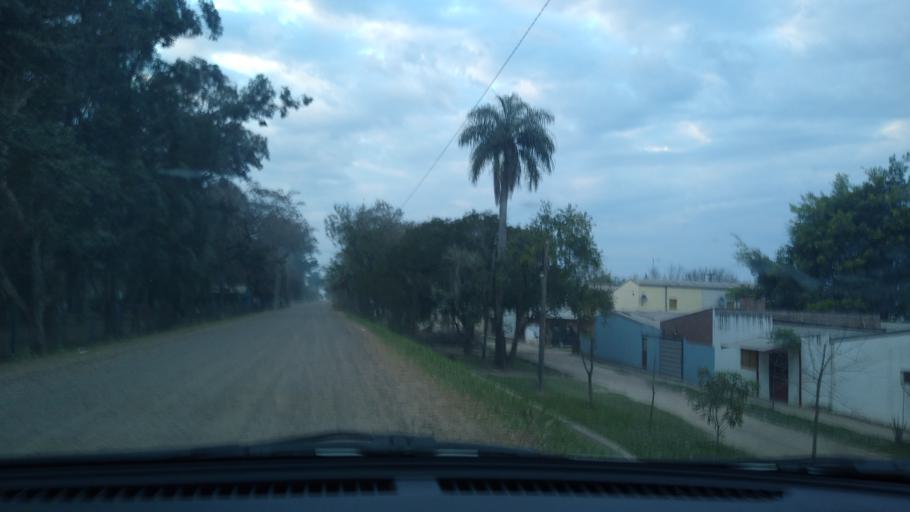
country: AR
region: Chaco
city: Barranqueras
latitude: -27.4599
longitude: -58.9479
